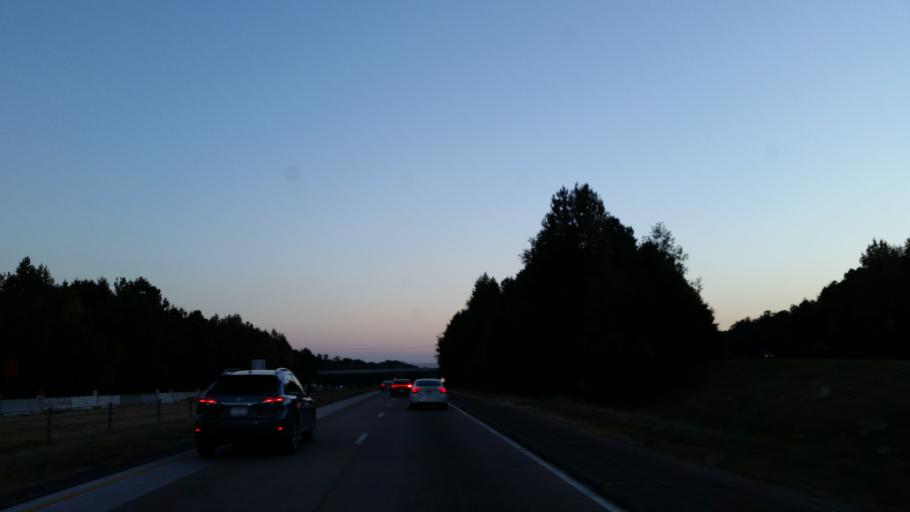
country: US
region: Georgia
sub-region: Forsyth County
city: Cumming
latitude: 34.2321
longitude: -84.1009
